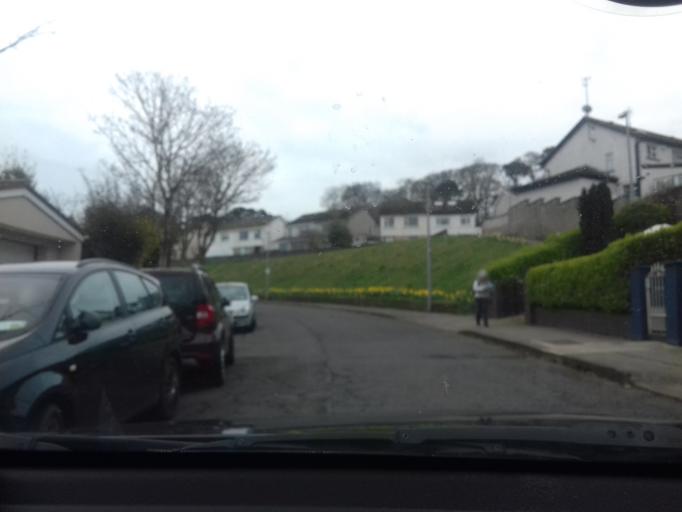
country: IE
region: Leinster
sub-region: Fingal County
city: Howth
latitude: 53.3819
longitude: -6.0709
